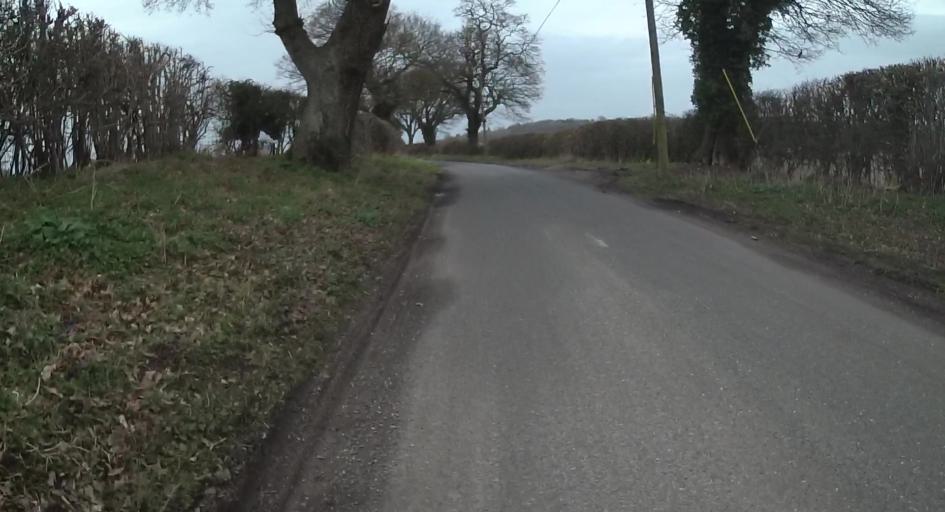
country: GB
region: England
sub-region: Hampshire
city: Overton
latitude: 51.2576
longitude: -1.1939
